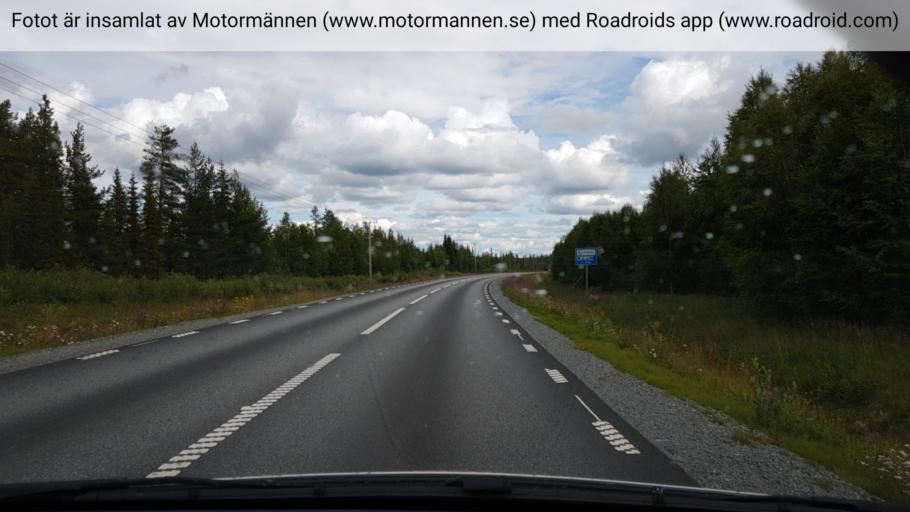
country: SE
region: Vaesterbotten
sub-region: Vilhelmina Kommun
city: Vilhelmina
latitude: 64.7893
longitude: 16.7758
